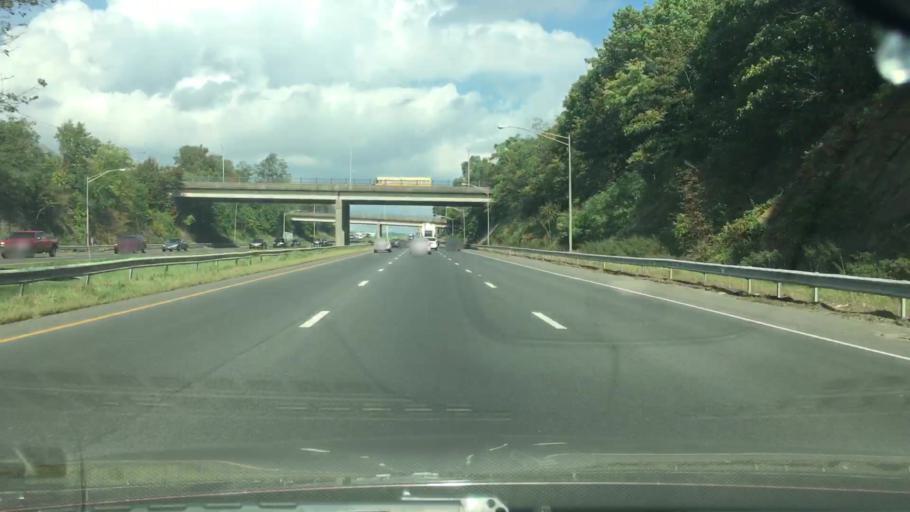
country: US
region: Connecticut
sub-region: Fairfield County
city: Bridgeport
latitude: 41.1804
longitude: -73.1943
